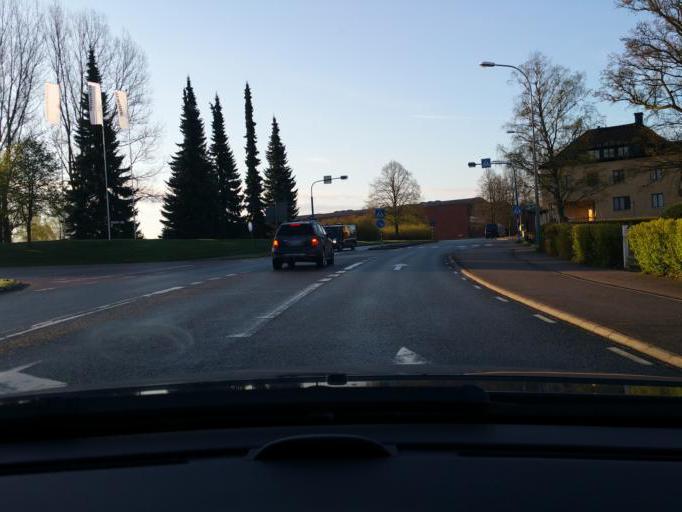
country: SE
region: Kronoberg
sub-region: Vaxjo Kommun
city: Lammhult
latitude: 57.1672
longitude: 14.5865
